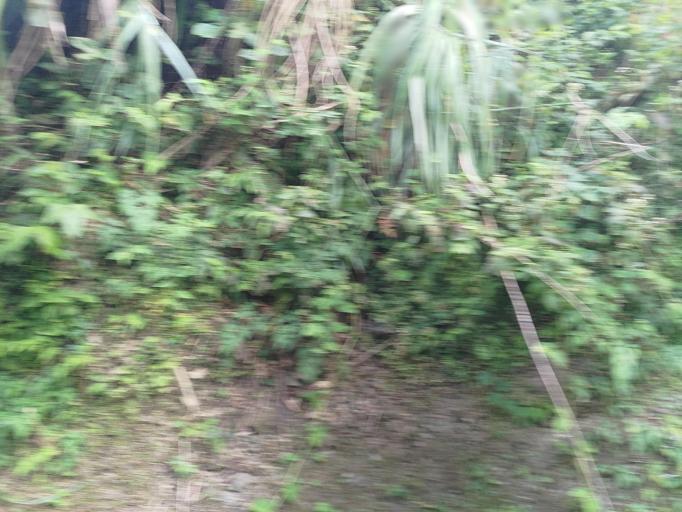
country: TW
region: Taiwan
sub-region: Hsinchu
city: Hsinchu
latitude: 24.6041
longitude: 121.0910
